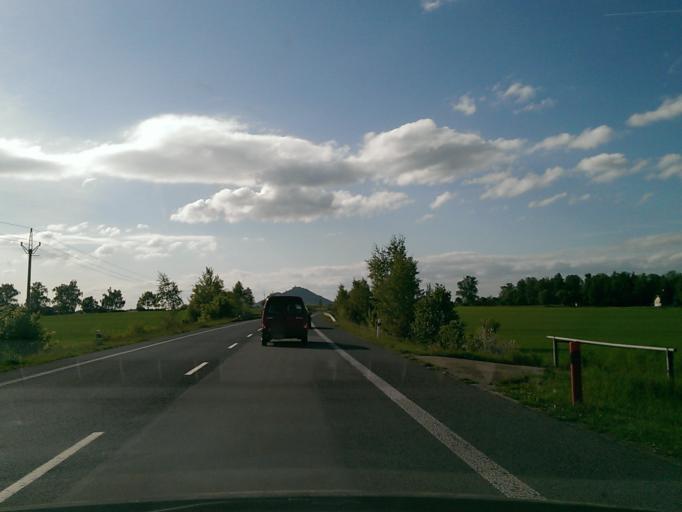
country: CZ
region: Central Bohemia
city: Bela pod Bezdezem
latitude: 50.4967
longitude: 14.7961
